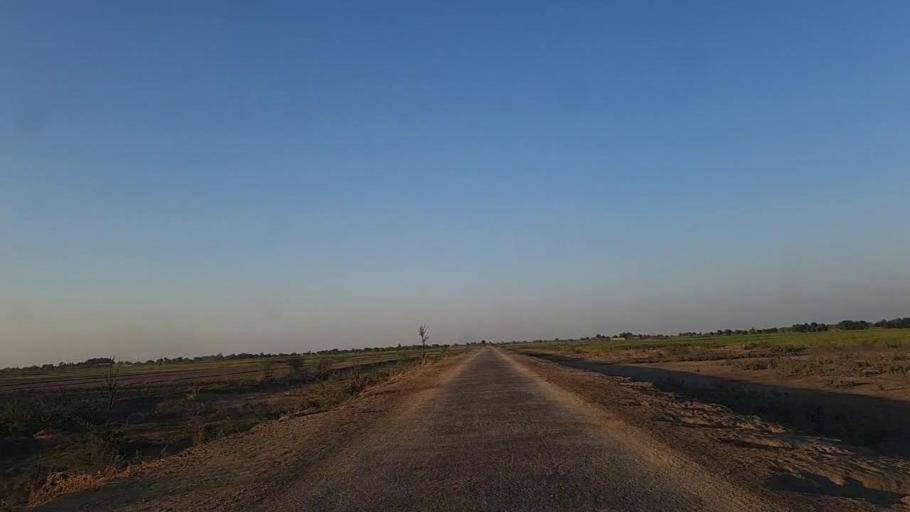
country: PK
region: Sindh
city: Naukot
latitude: 25.0204
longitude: 69.4167
